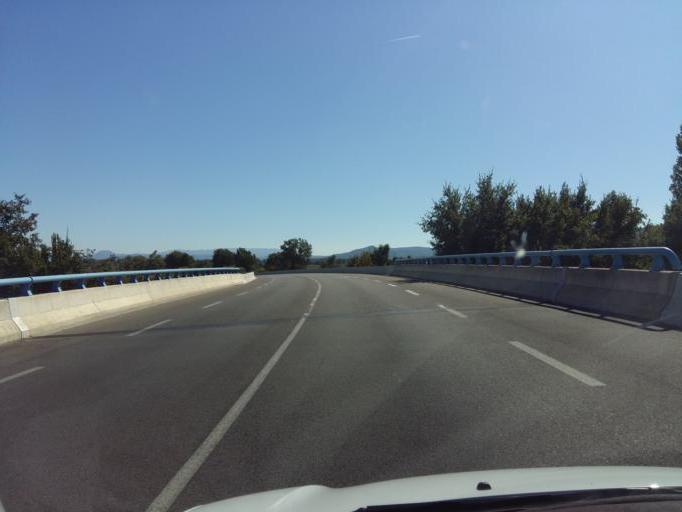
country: FR
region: Provence-Alpes-Cote d'Azur
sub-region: Departement du Vaucluse
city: Cadenet
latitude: 43.7234
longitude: 5.3848
